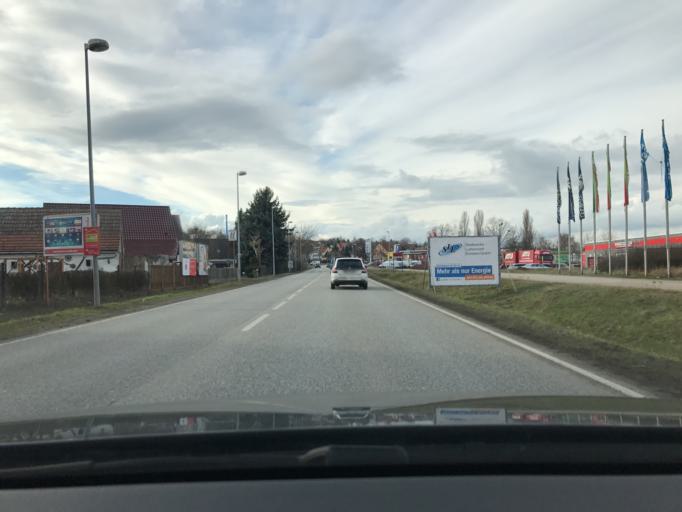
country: DE
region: Saxony-Anhalt
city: Volkstedt
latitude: 51.5112
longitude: 11.5734
